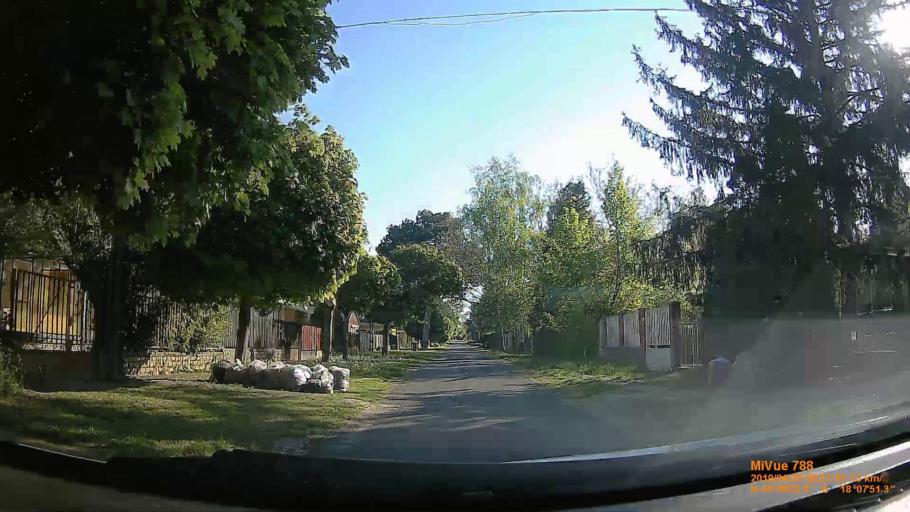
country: HU
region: Somogy
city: Balatonszabadi
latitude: 46.9397
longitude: 18.1311
